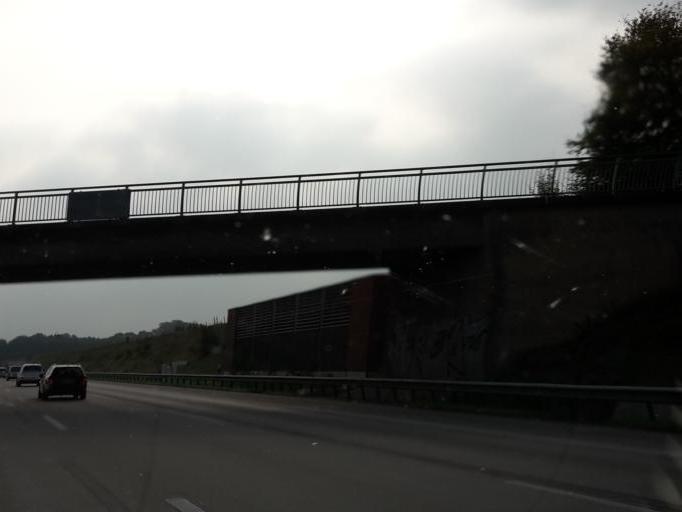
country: DE
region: Lower Saxony
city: Buehren
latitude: 52.8390
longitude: 8.2187
